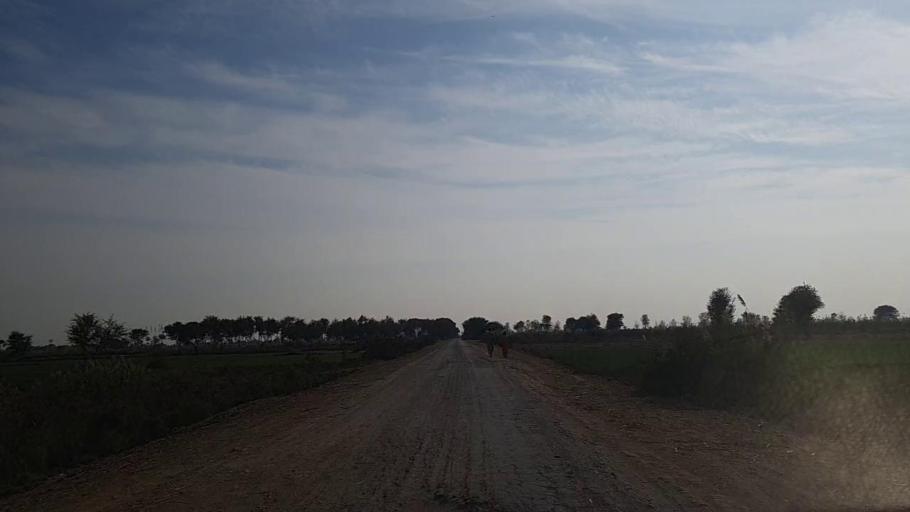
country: PK
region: Sindh
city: Daur
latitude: 26.4656
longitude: 68.4175
